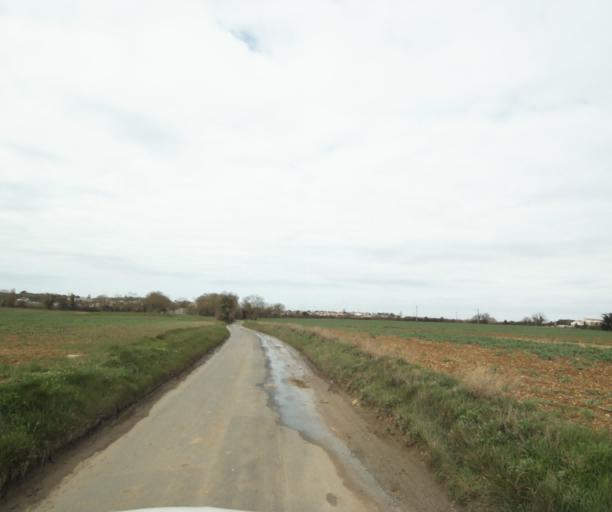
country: FR
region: Poitou-Charentes
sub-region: Departement de la Charente-Maritime
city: Nieul-sur-Mer
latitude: 46.1904
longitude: -1.1724
